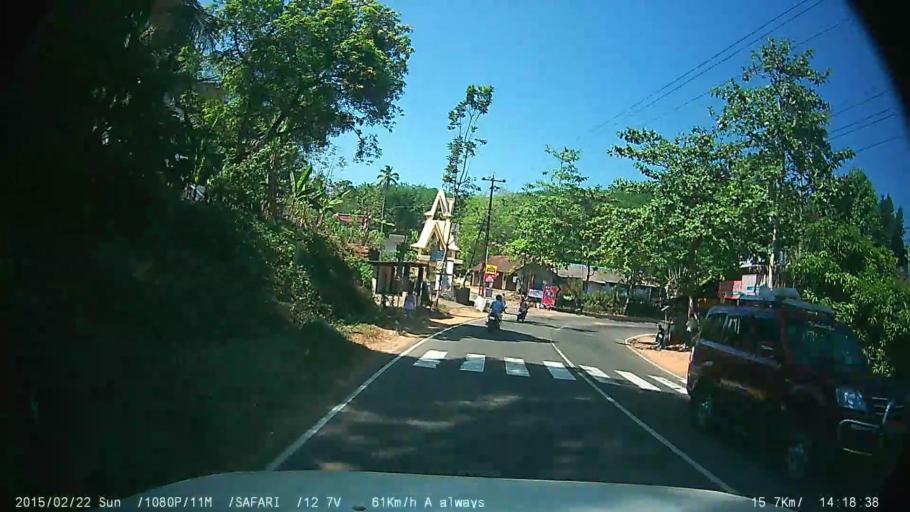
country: IN
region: Kerala
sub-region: Kottayam
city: Lalam
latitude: 9.5660
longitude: 76.6872
